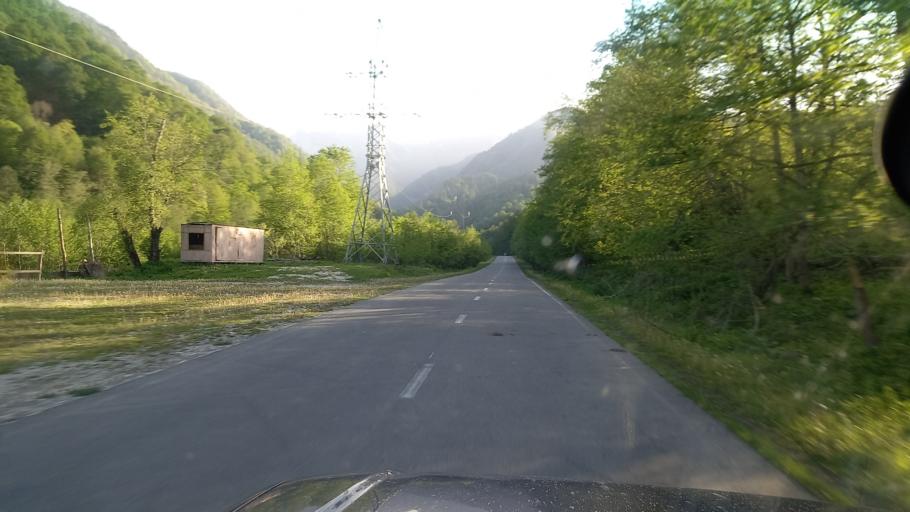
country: RU
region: North Ossetia
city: Tarskoye
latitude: 42.9054
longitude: 44.9572
